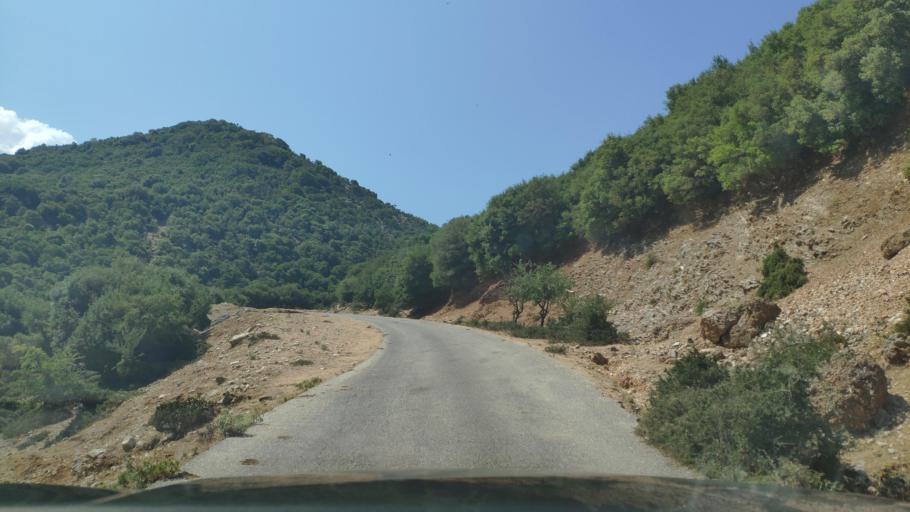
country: GR
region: West Greece
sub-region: Nomos Aitolias kai Akarnanias
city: Monastirakion
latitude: 38.8339
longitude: 20.9326
